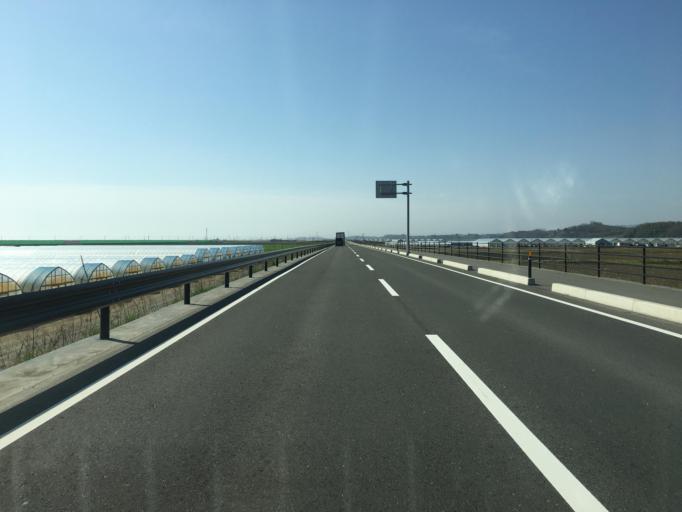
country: JP
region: Miyagi
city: Watari
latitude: 37.9552
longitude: 140.9046
